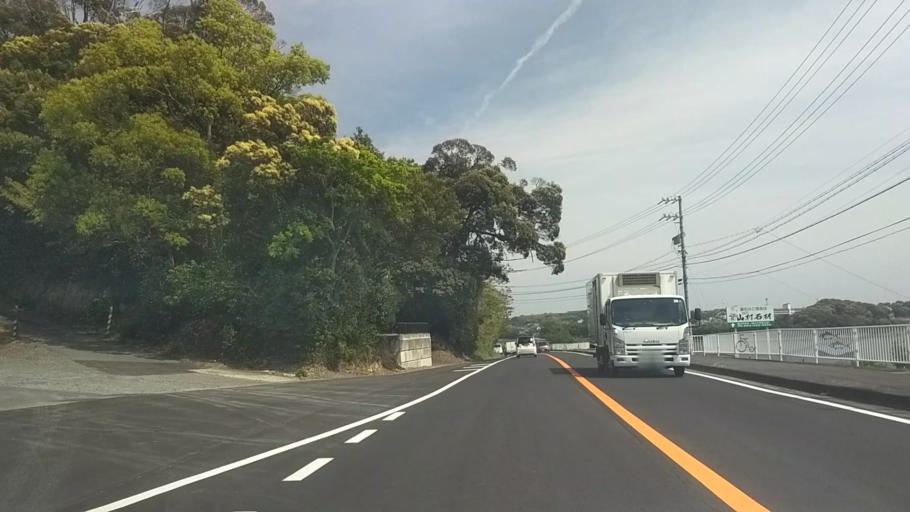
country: JP
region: Shizuoka
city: Kosai-shi
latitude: 34.7970
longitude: 137.5640
